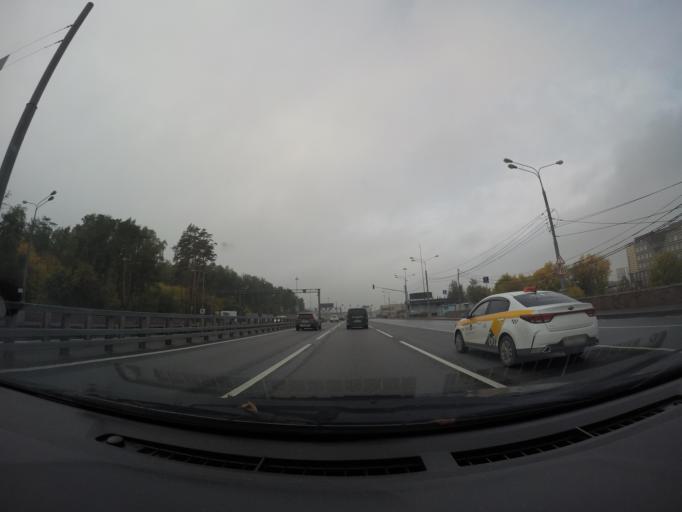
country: RU
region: Moscow
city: Rublevo
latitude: 55.7883
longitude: 37.3809
